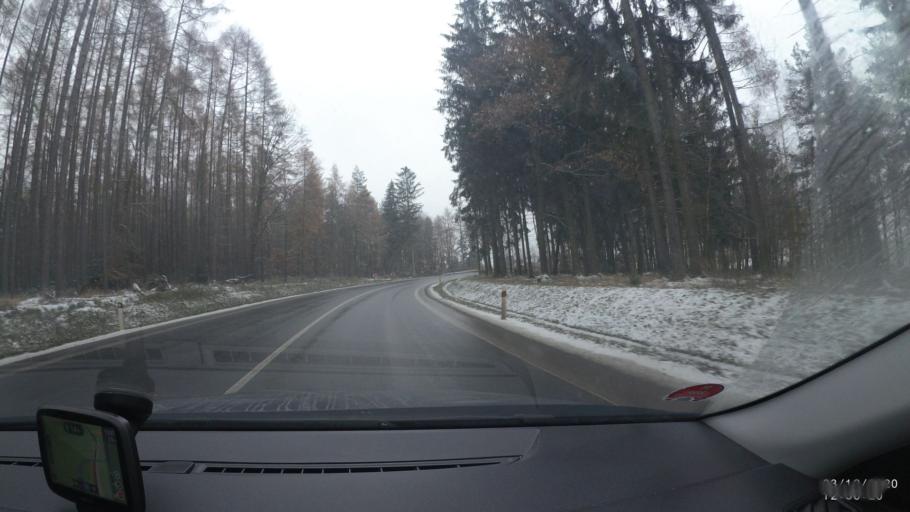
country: CZ
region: Central Bohemia
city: Nove Straseci
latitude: 50.1656
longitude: 13.8799
